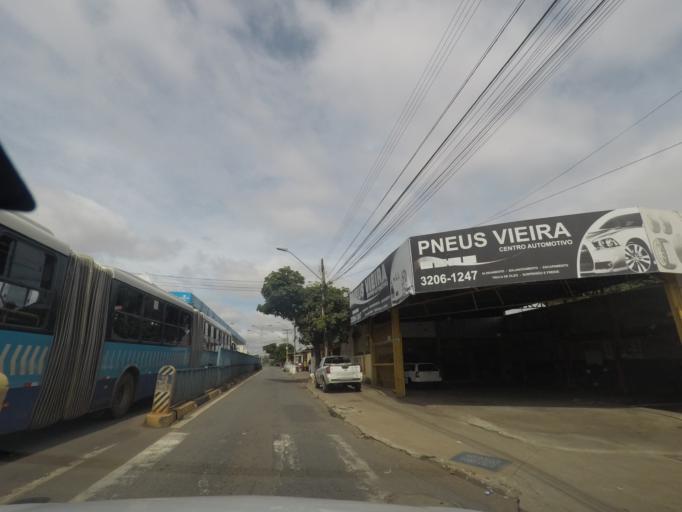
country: BR
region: Goias
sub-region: Goiania
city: Goiania
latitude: -16.6682
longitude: -49.2158
